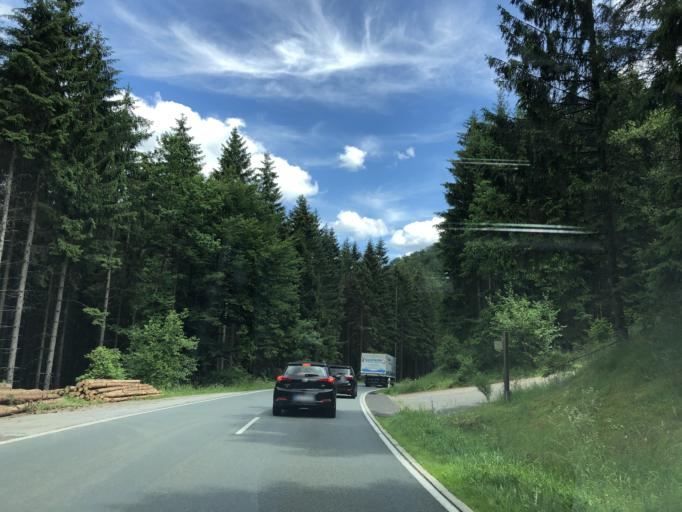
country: DE
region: North Rhine-Westphalia
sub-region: Regierungsbezirk Arnsberg
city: Kirchhundem
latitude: 51.1092
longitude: 8.1382
